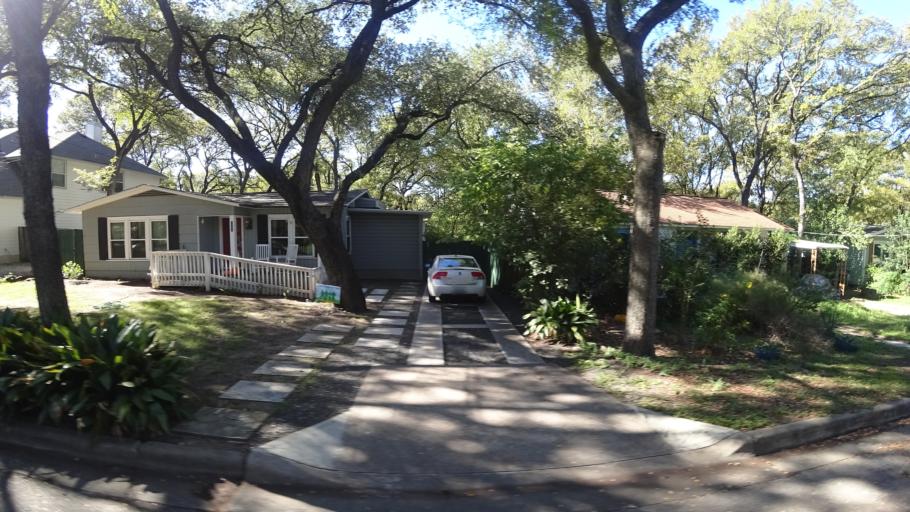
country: US
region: Texas
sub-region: Travis County
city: Rollingwood
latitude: 30.2828
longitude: -97.7732
